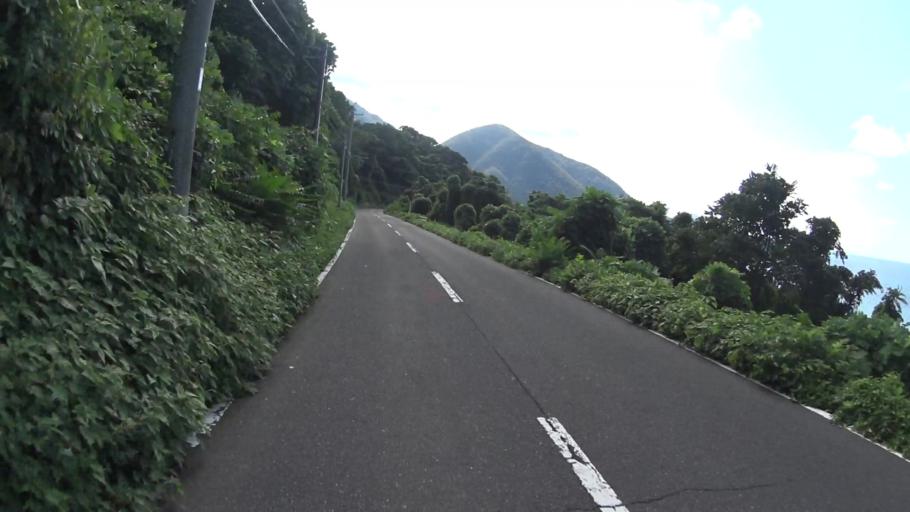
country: JP
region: Kyoto
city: Miyazu
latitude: 35.7670
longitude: 135.2148
